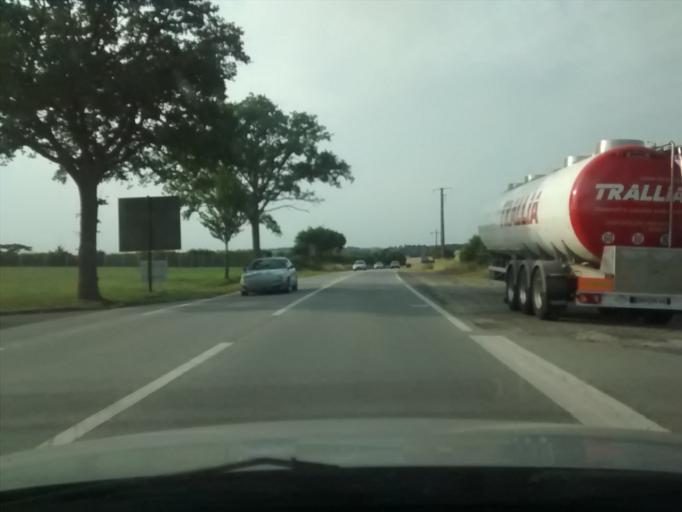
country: FR
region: Brittany
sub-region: Departement d'Ille-et-Vilaine
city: Etrelles
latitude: 48.0739
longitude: -1.2000
